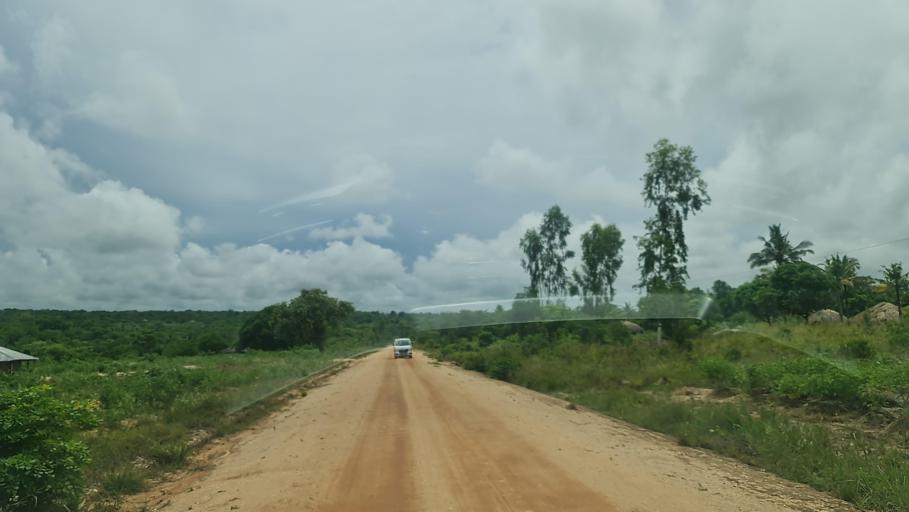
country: MZ
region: Zambezia
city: Quelimane
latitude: -17.2676
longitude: 37.2478
